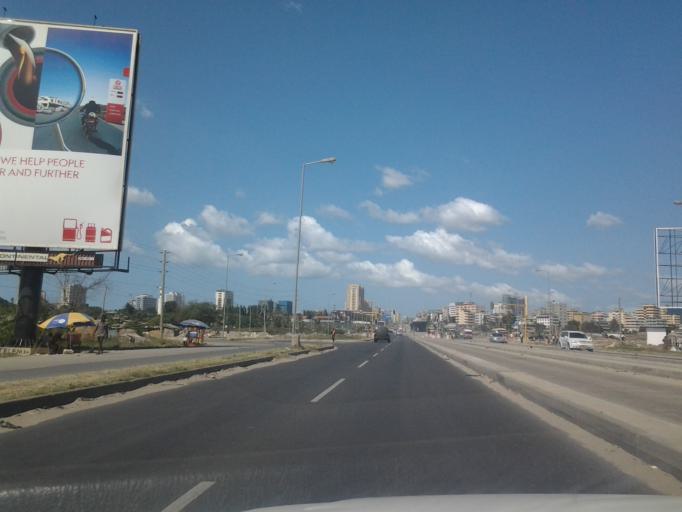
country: TZ
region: Dar es Salaam
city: Dar es Salaam
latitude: -6.8103
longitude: 39.2660
